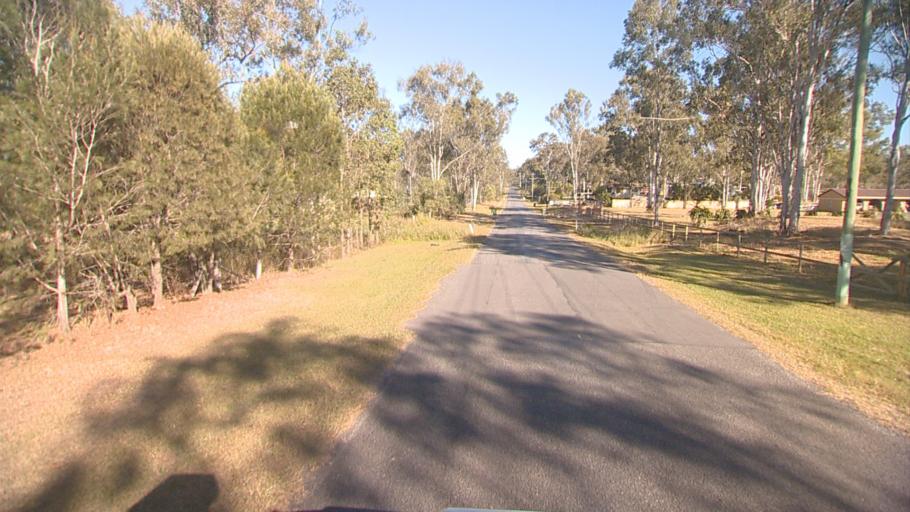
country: AU
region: Queensland
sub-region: Logan
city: Park Ridge South
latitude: -27.7227
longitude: 152.9912
